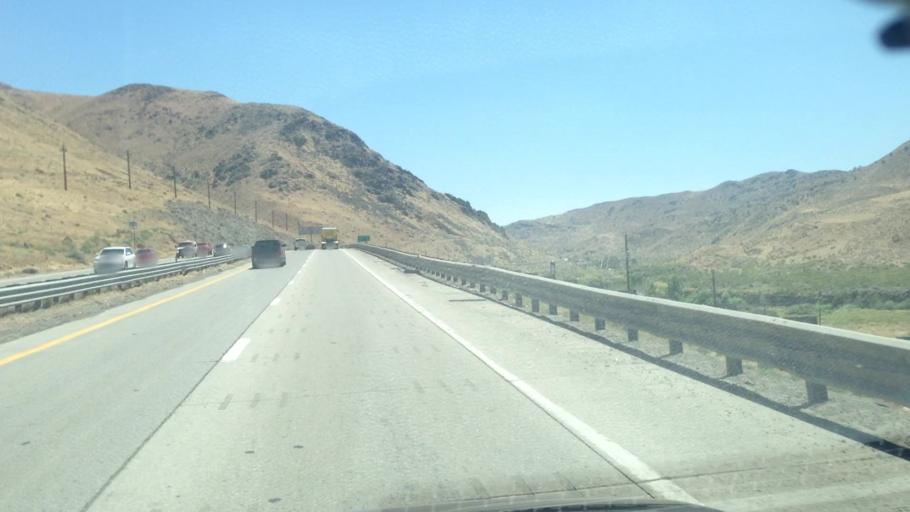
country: US
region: Nevada
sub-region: Washoe County
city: Sparks
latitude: 39.5241
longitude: -119.6939
